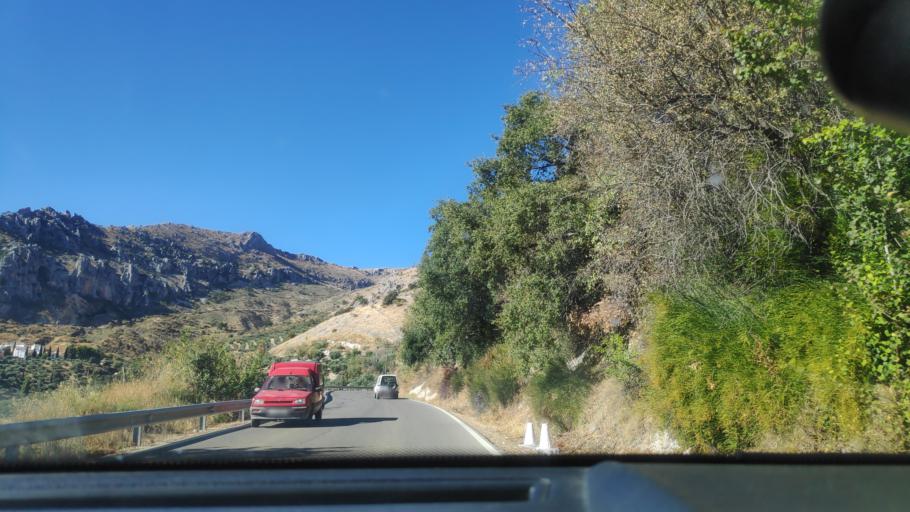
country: ES
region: Andalusia
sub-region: Provincia de Jaen
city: Jimena
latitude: 37.8006
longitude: -3.4649
